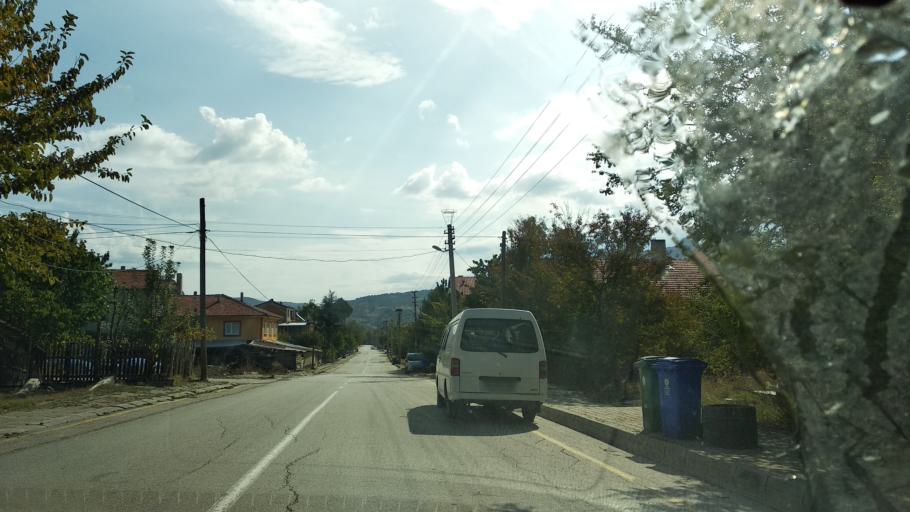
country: TR
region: Bolu
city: Seben
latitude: 40.4134
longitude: 31.5670
